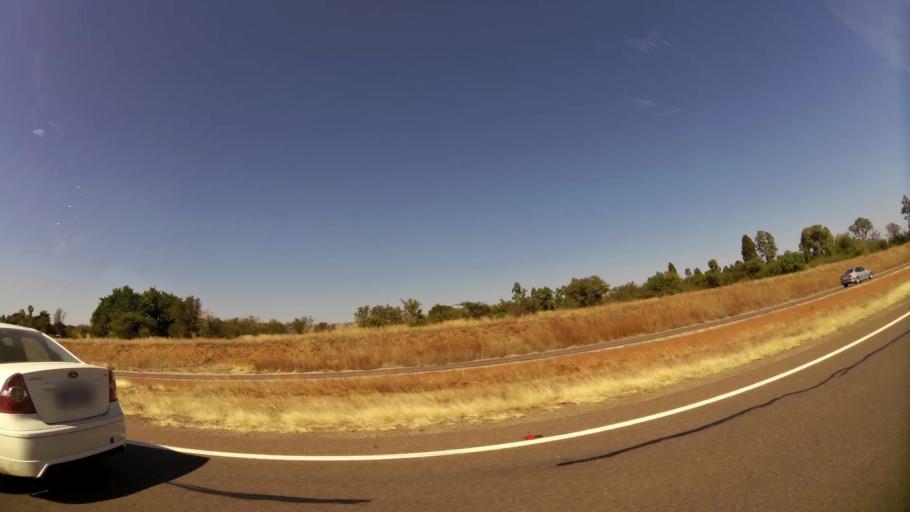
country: ZA
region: North-West
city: Ga-Rankuwa
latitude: -25.6574
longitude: 28.0770
